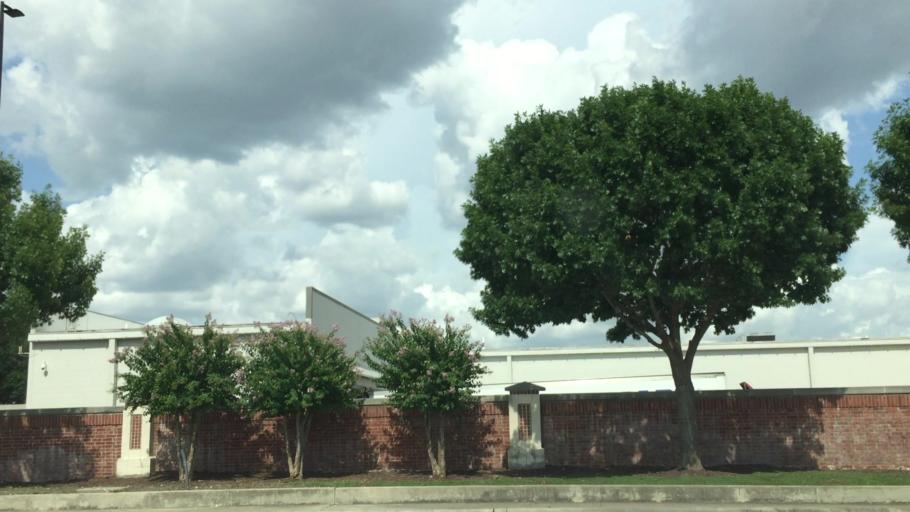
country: US
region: Texas
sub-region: Harris County
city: Bunker Hill Village
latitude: 29.7338
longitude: -95.5925
